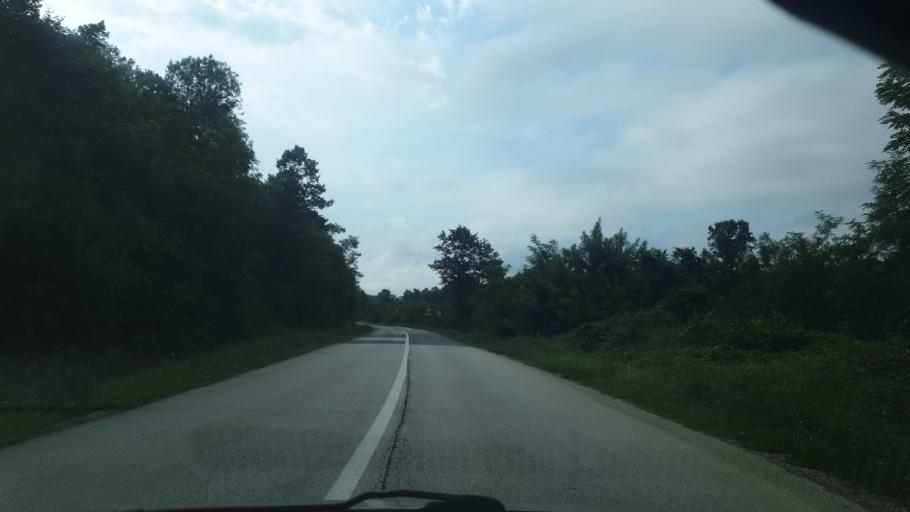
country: RS
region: Central Serbia
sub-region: Sumadijski Okrug
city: Topola
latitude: 44.2278
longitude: 20.7120
